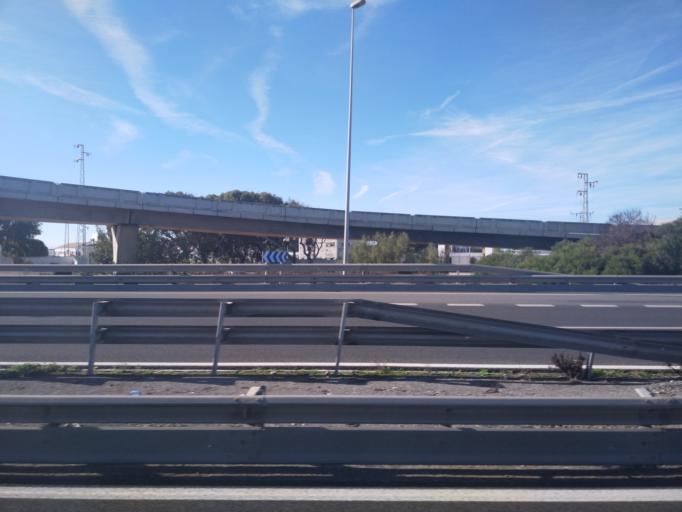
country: ES
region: Andalusia
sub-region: Provincia de Cadiz
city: San Fernando
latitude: 36.4615
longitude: -6.2513
